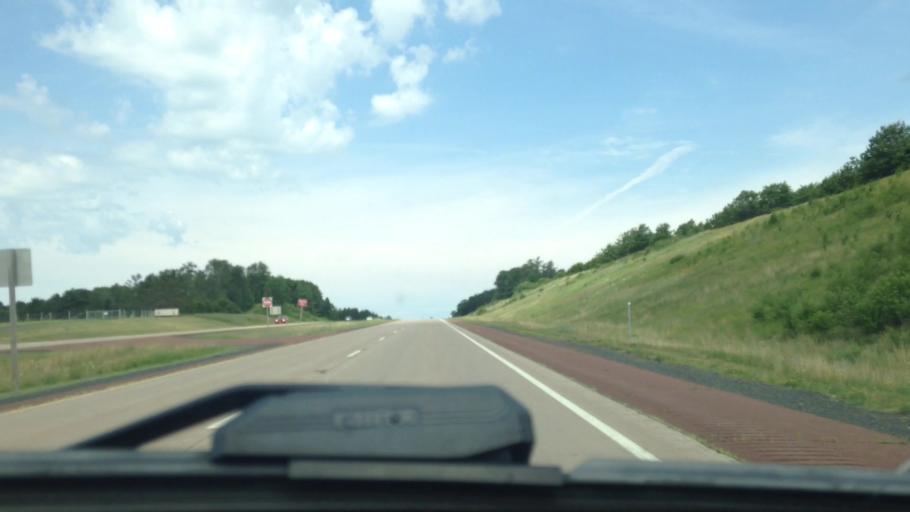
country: US
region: Wisconsin
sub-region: Douglas County
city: Lake Nebagamon
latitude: 46.3291
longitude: -91.8220
